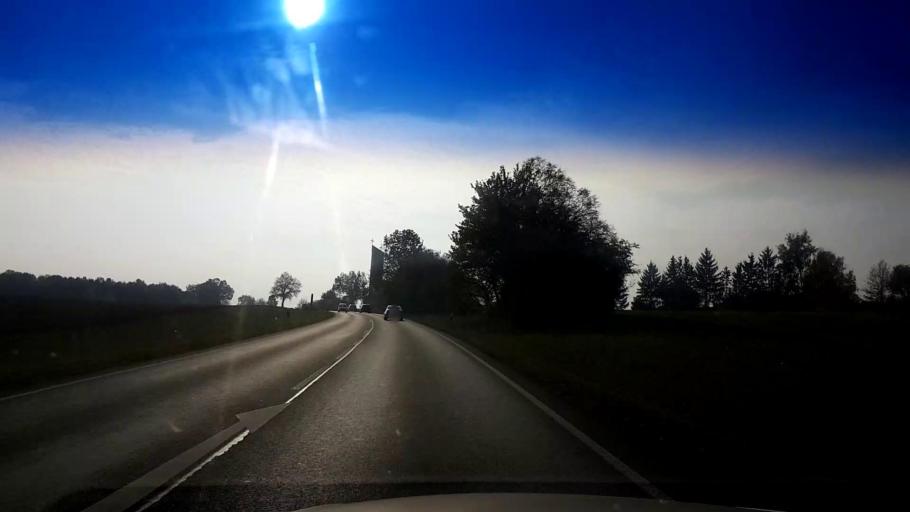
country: DE
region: Bavaria
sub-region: Upper Franconia
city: Himmelkron
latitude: 50.0616
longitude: 11.6042
